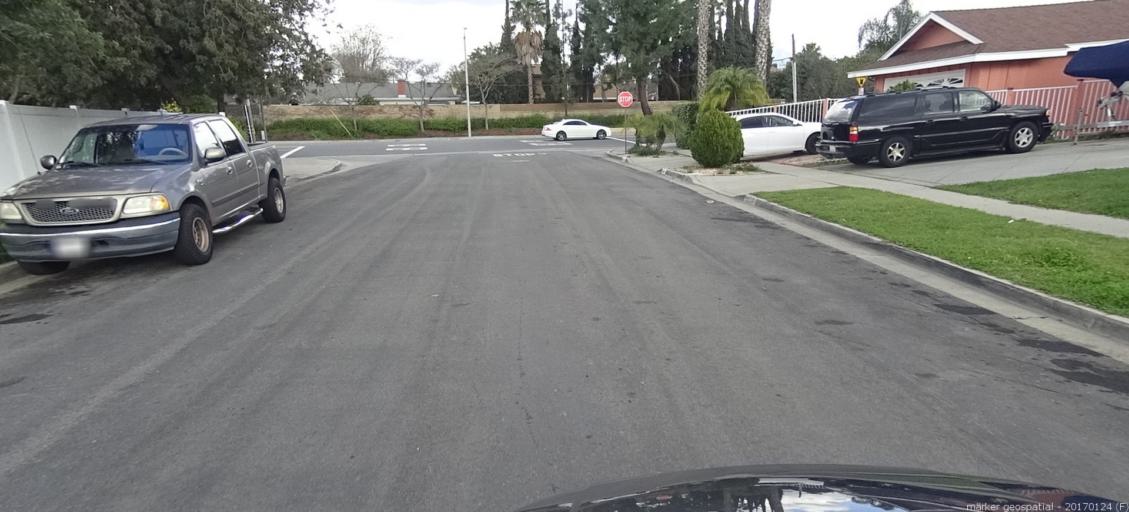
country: US
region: California
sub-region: Orange County
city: Laguna Hills
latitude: 33.6238
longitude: -117.6989
